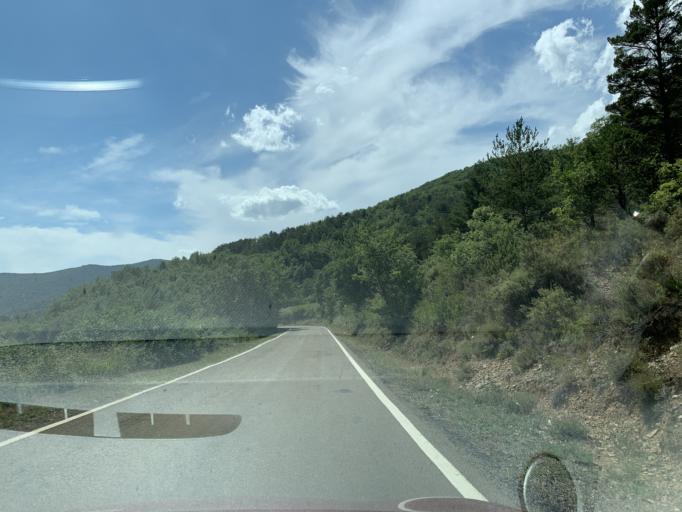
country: ES
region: Aragon
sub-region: Provincia de Huesca
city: Jasa
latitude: 42.6279
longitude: -0.6522
